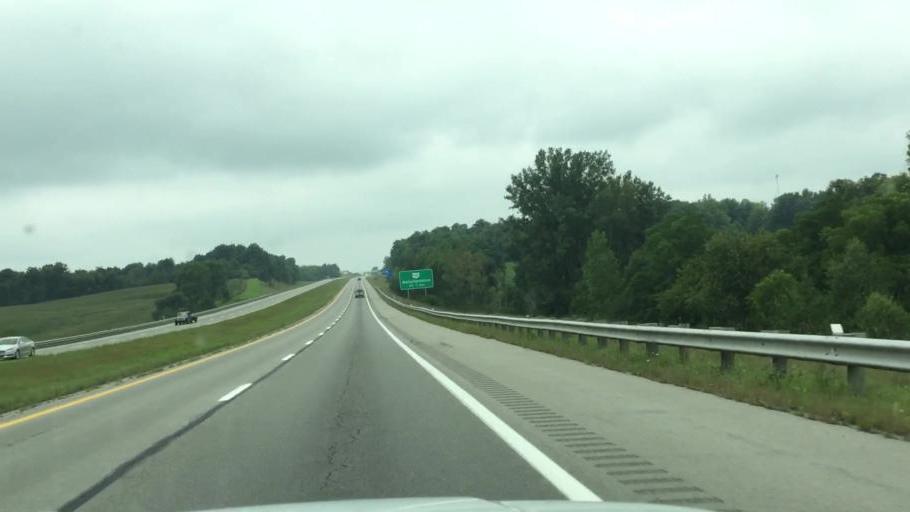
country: US
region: Ohio
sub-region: Logan County
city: Bellefontaine
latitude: 40.3561
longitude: -83.7114
